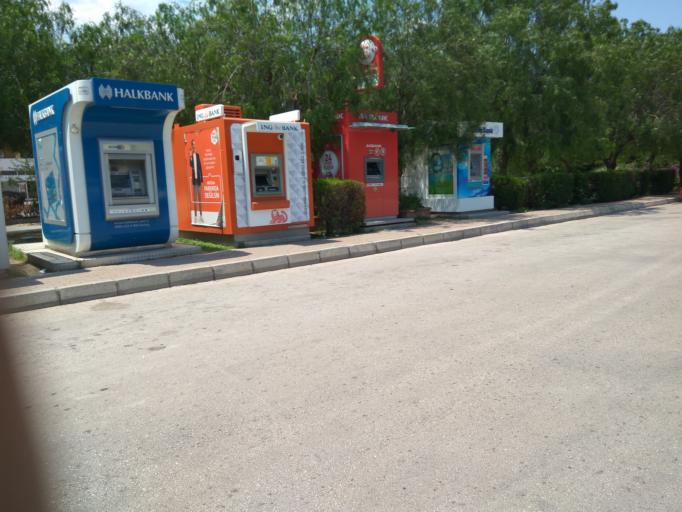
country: TR
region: Antalya
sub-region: Kemer
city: Goeynuek
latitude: 36.6674
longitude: 30.5517
